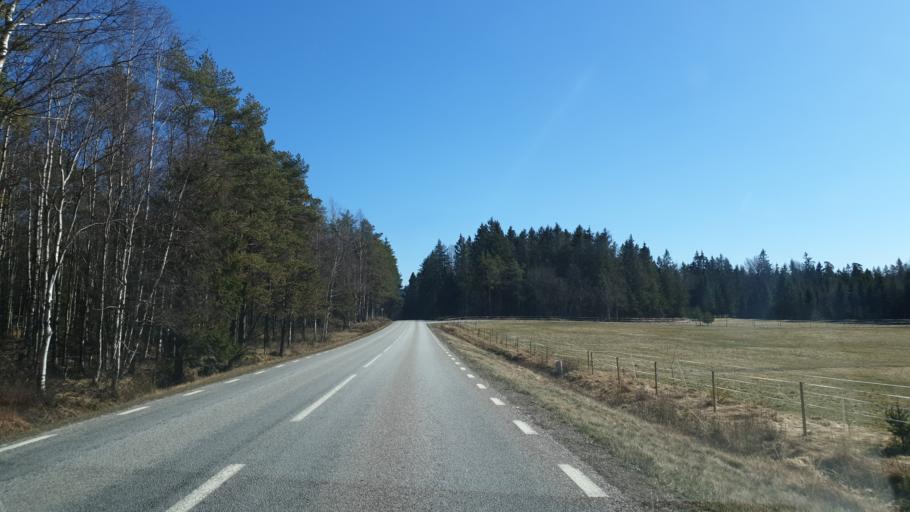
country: SE
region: Vaestra Goetaland
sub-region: Tanums Kommun
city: Tanumshede
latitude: 58.7420
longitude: 11.4661
